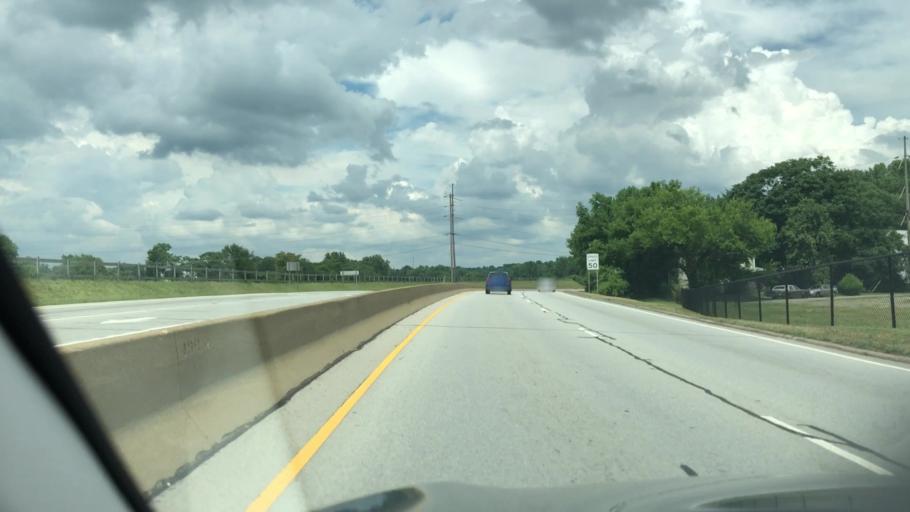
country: US
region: Ohio
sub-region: Stark County
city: Massillon
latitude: 40.8006
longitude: -81.5285
